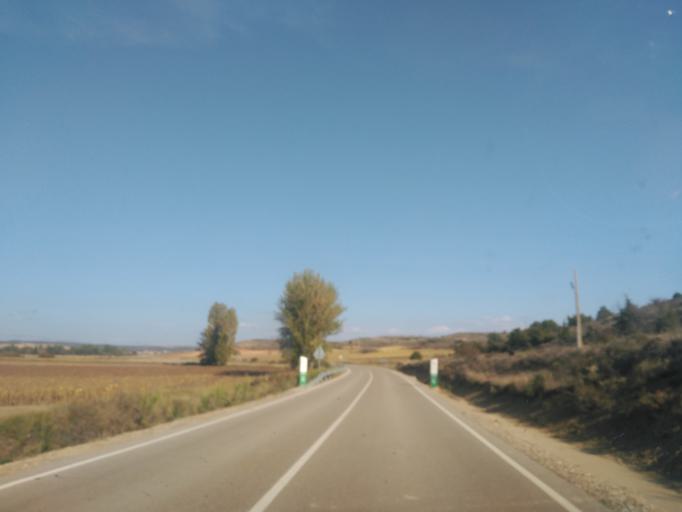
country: ES
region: Castille and Leon
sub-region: Provincia de Soria
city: Alcubilla de Avellaneda
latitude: 41.7550
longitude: -3.2583
